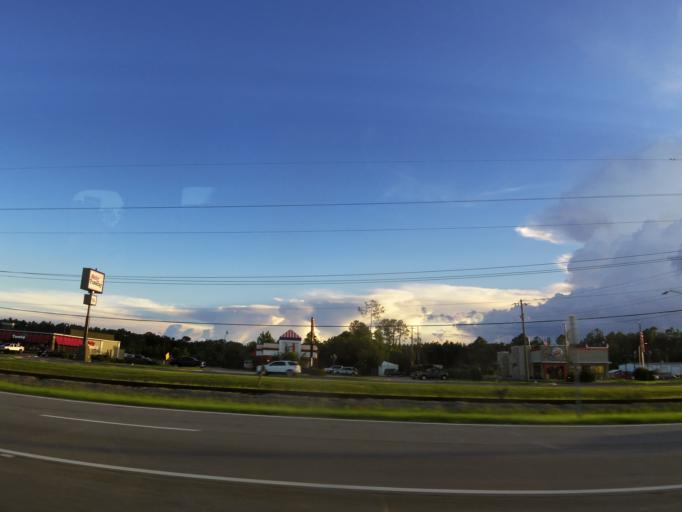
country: US
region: Georgia
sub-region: Camden County
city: Kingsland
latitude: 30.7889
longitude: -81.6532
